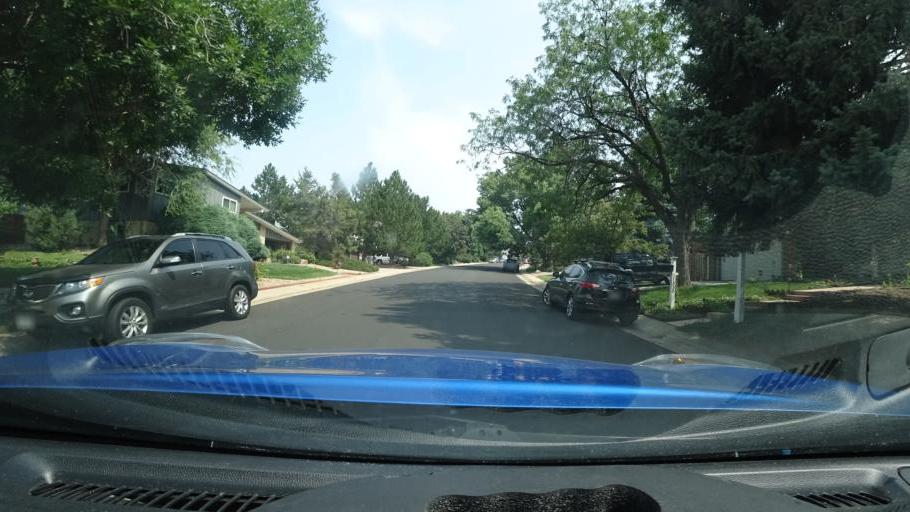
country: US
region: Colorado
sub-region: Adams County
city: Aurora
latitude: 39.6722
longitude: -104.8597
